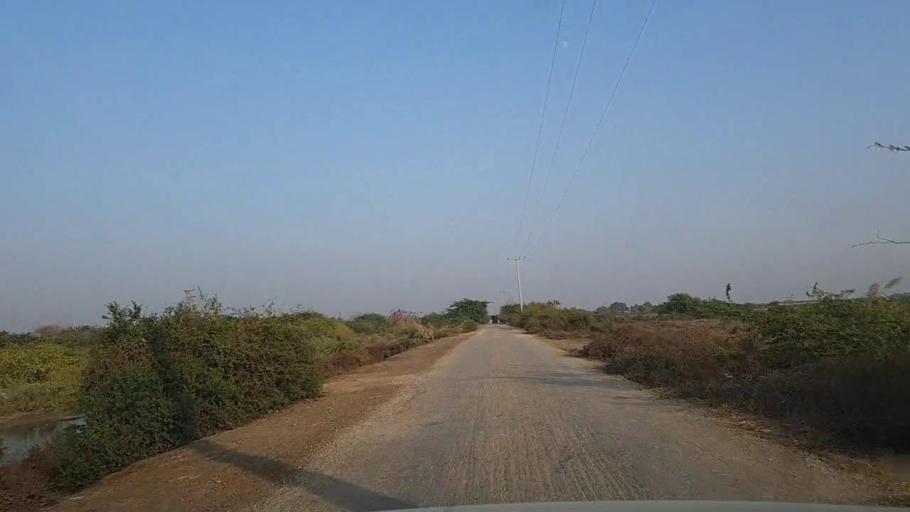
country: PK
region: Sindh
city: Keti Bandar
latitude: 24.2805
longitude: 67.6202
